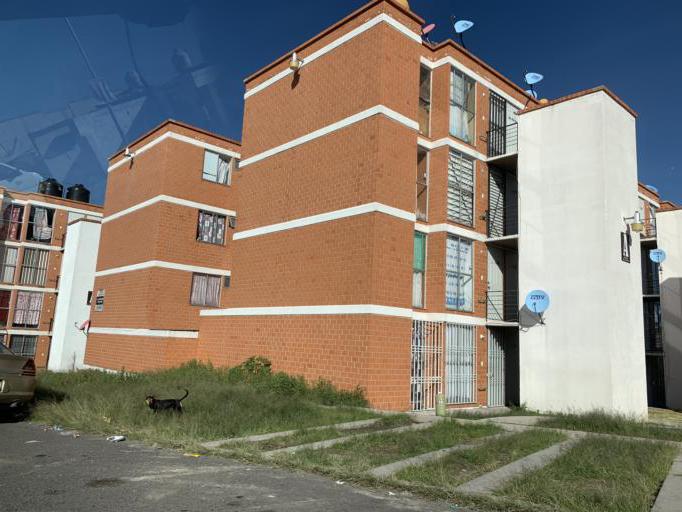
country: MX
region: Puebla
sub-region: Puebla
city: El Capulo (La Quebradora)
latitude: 18.9525
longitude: -98.2534
